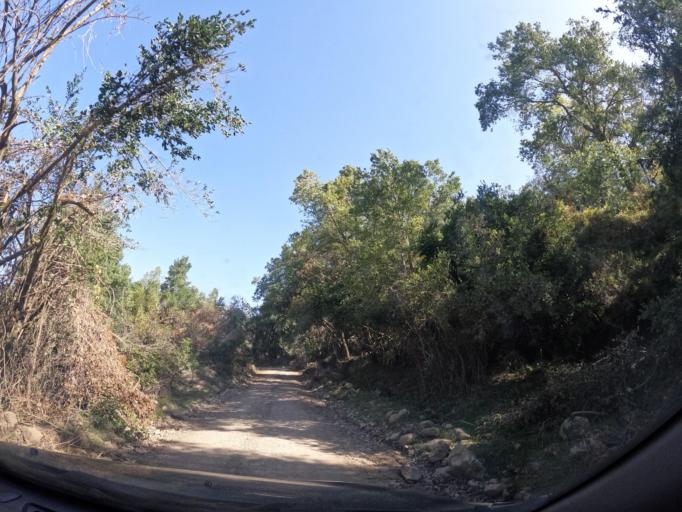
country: CL
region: Maule
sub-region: Provincia de Linares
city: Longavi
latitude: -36.2787
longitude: -71.4162
